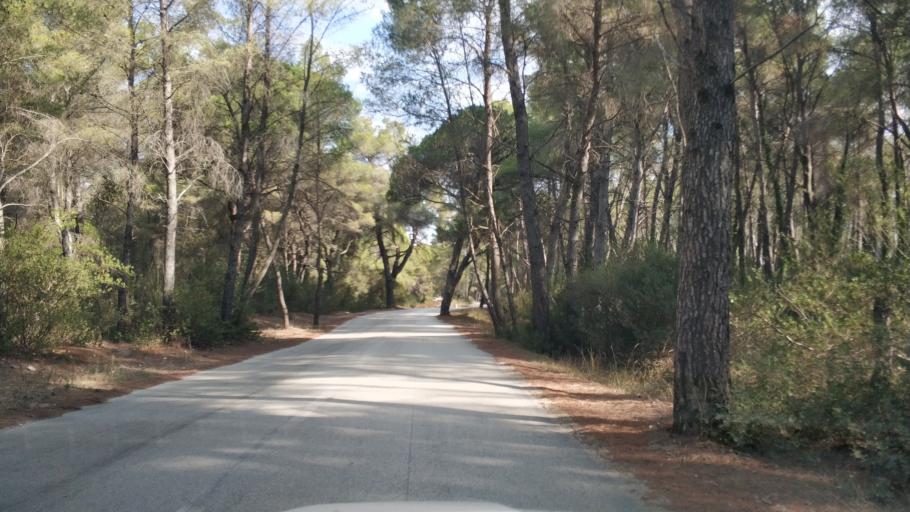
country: AL
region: Fier
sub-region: Rrethi i Lushnjes
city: Divjake
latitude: 40.9783
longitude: 19.4816
